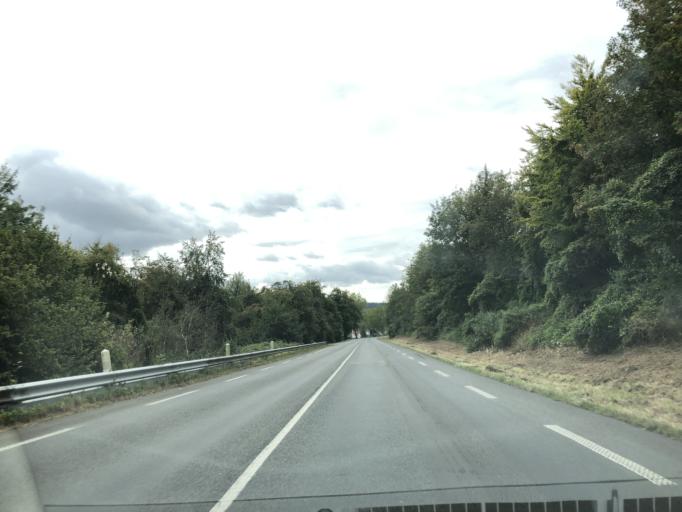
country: FR
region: Nord-Pas-de-Calais
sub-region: Departement du Pas-de-Calais
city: Marconne
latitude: 50.3889
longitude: 2.0483
